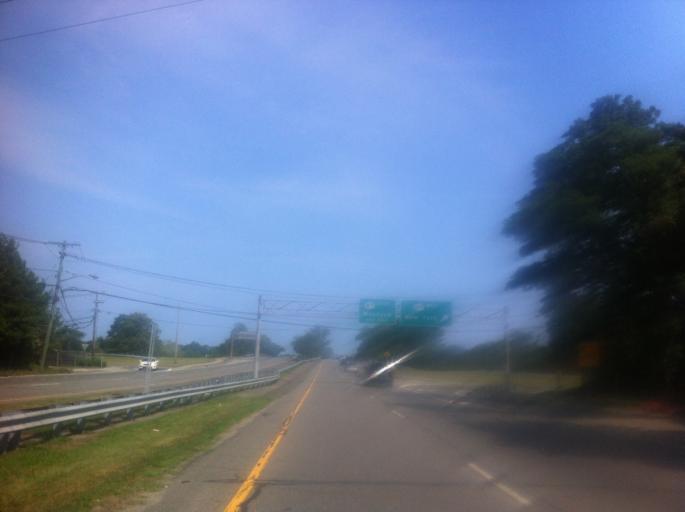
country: US
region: New York
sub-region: Suffolk County
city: North Lindenhurst
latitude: 40.7131
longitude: -73.3748
